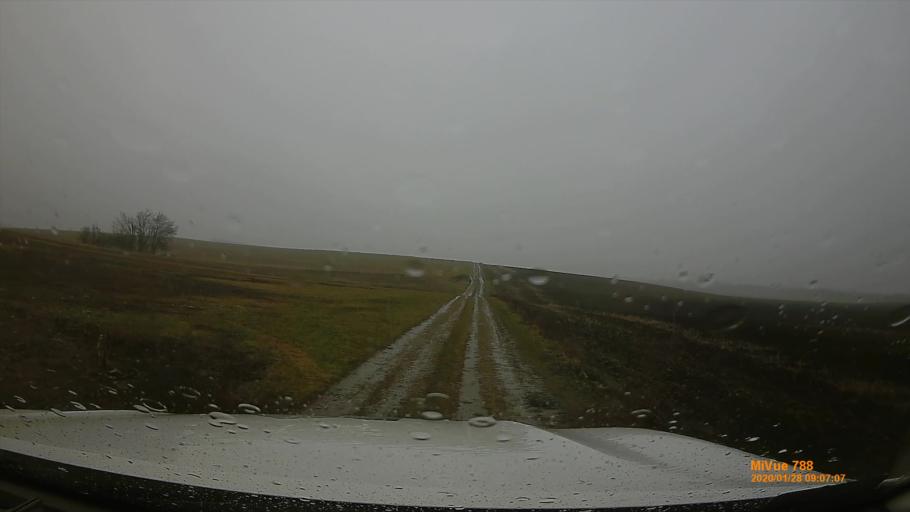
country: HU
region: Pest
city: Pilis
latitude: 47.3175
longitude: 19.5387
